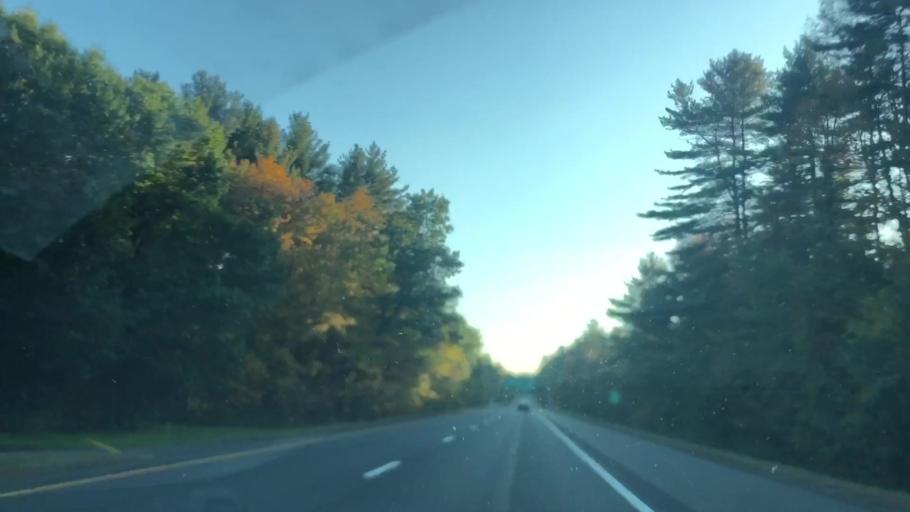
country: US
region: Massachusetts
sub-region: Franklin County
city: Turners Falls
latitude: 42.6276
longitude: -72.5845
